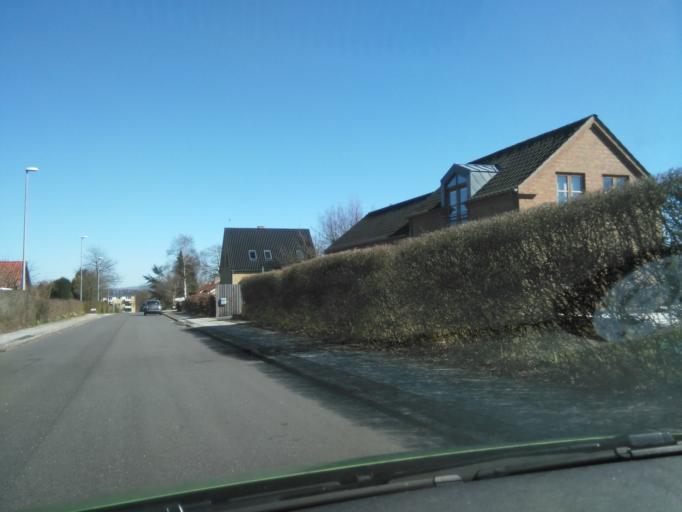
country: DK
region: Central Jutland
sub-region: Arhus Kommune
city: Lystrup
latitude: 56.1967
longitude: 10.2277
